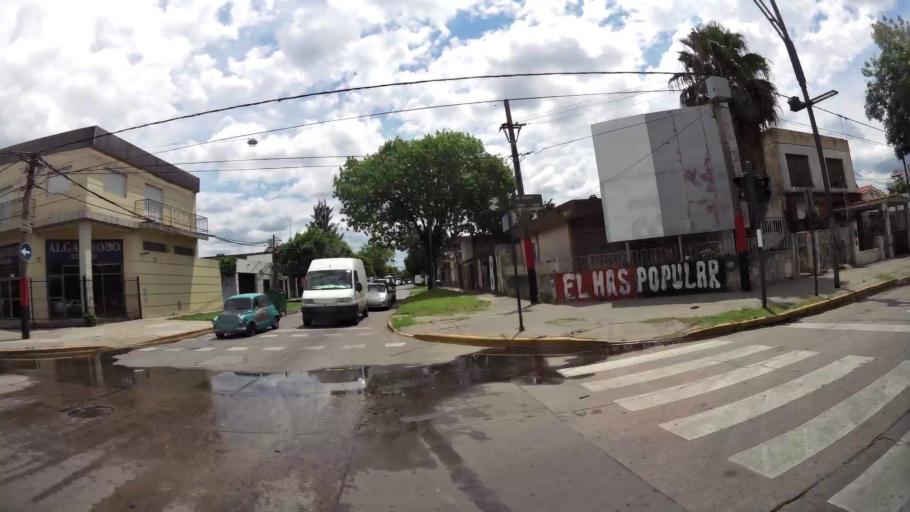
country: AR
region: Santa Fe
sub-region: Departamento de Rosario
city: Rosario
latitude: -32.9786
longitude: -60.6622
